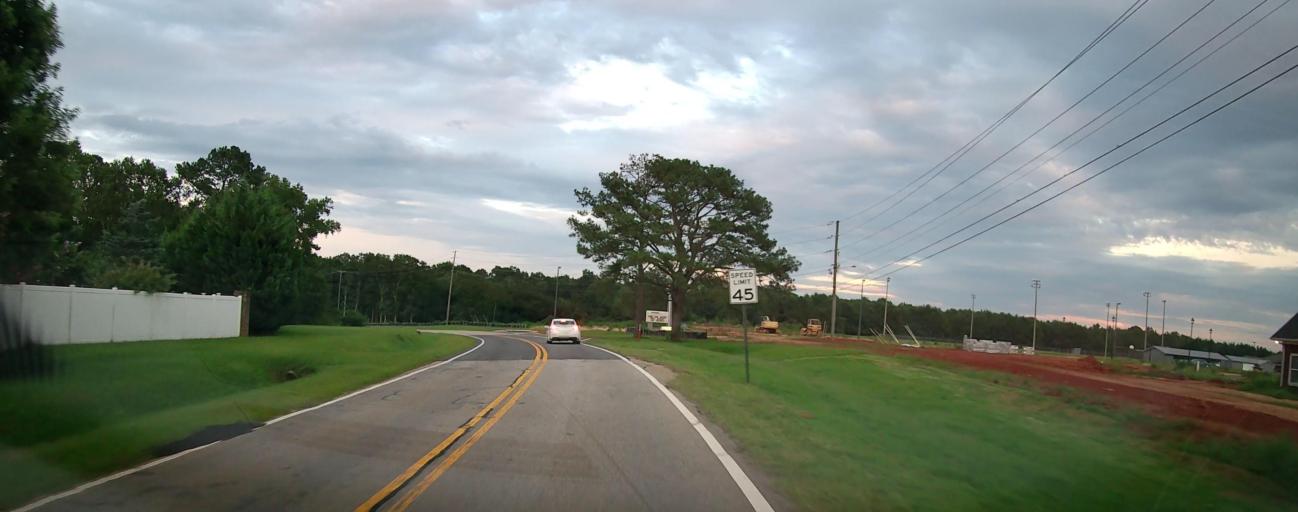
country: US
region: Georgia
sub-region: Houston County
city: Centerville
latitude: 32.6188
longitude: -83.7213
